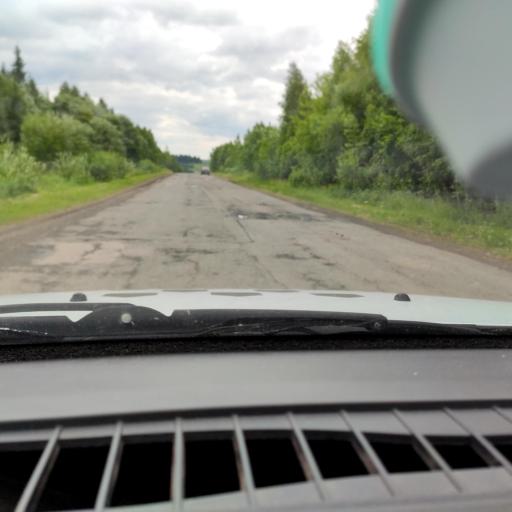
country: RU
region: Perm
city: Uinskoye
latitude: 57.1250
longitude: 56.5554
